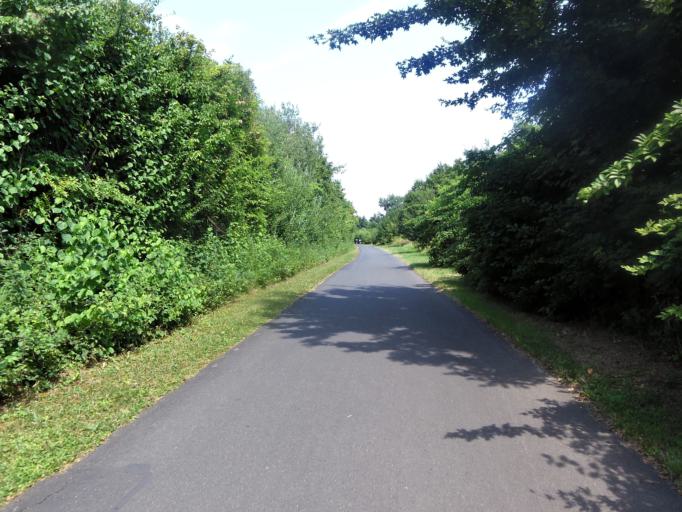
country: DE
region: Bavaria
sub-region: Regierungsbezirk Unterfranken
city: Zell am Main
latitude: 49.8190
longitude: 9.8715
